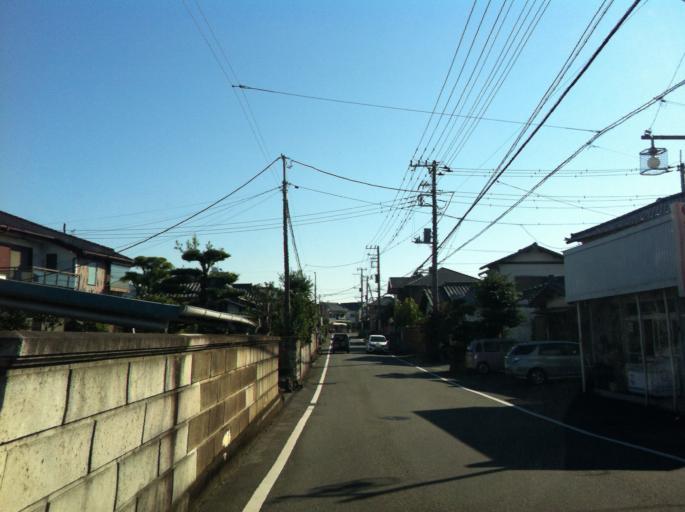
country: JP
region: Shizuoka
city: Fuji
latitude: 35.1649
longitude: 138.7298
